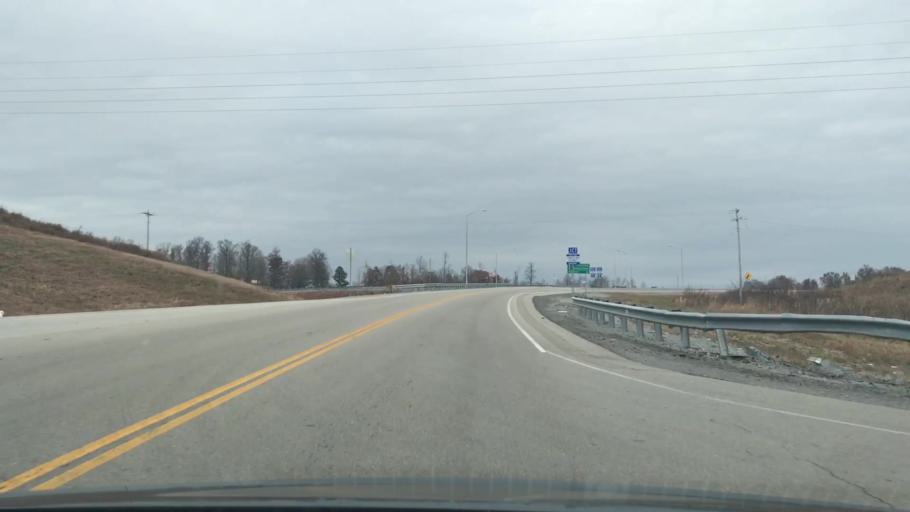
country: US
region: Kentucky
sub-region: Metcalfe County
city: Edmonton
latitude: 36.9977
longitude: -85.6159
